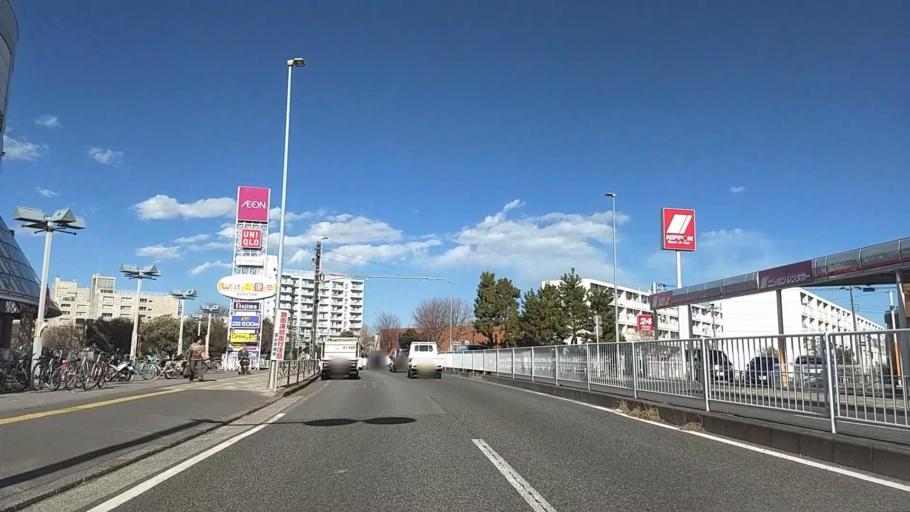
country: JP
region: Kanagawa
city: Zushi
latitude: 35.3331
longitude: 139.6230
